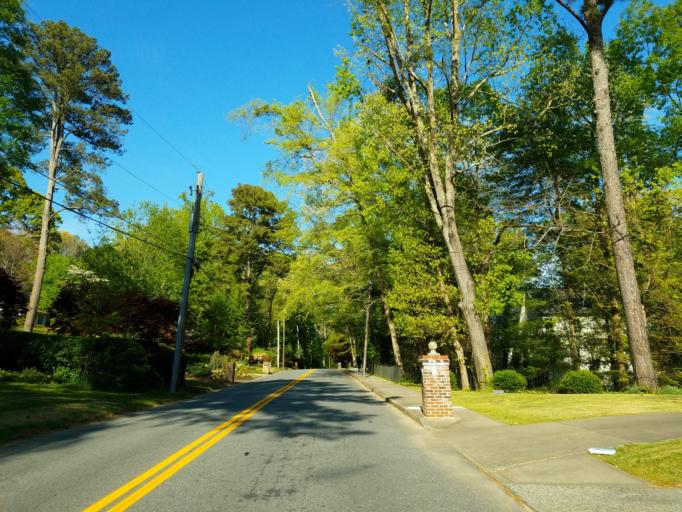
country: US
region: Georgia
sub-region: Cobb County
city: Vinings
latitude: 33.8271
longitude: -84.4366
